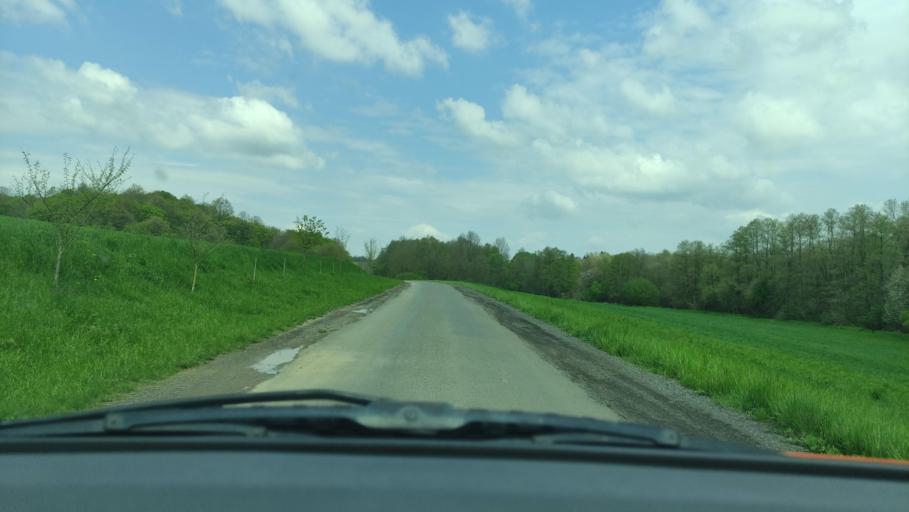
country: HU
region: Baranya
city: Sasd
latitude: 46.2816
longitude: 18.1054
